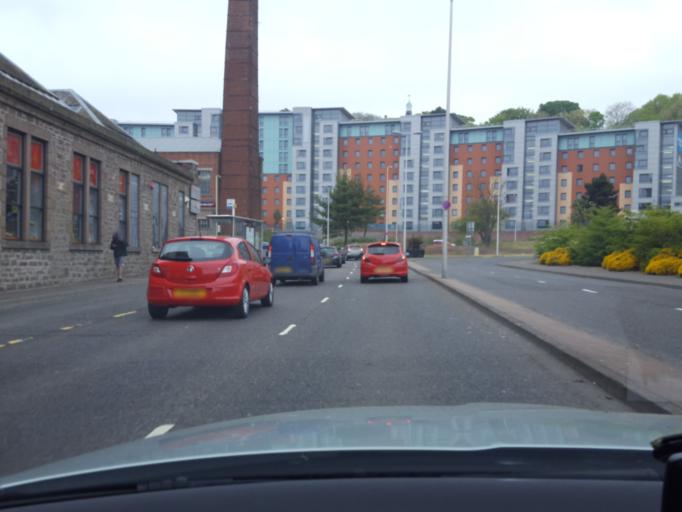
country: GB
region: Scotland
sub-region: Dundee City
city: Dundee
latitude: 56.4627
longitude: -2.9791
